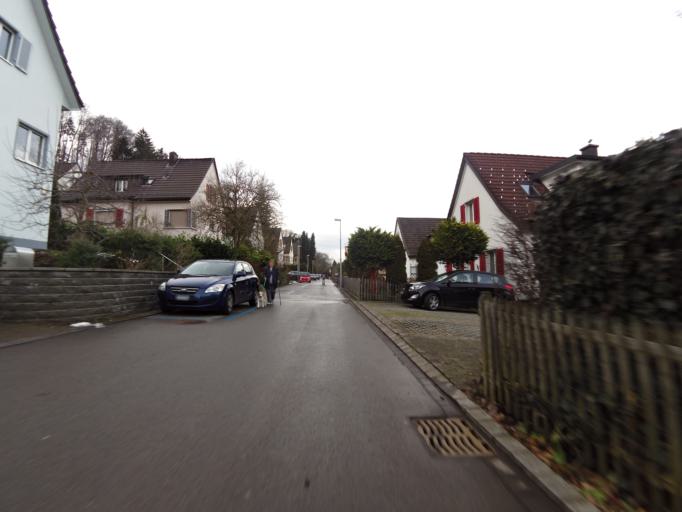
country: CH
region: Zurich
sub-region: Bezirk Zuerich
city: Zuerich (Kreis 9)
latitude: 47.3768
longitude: 8.4801
